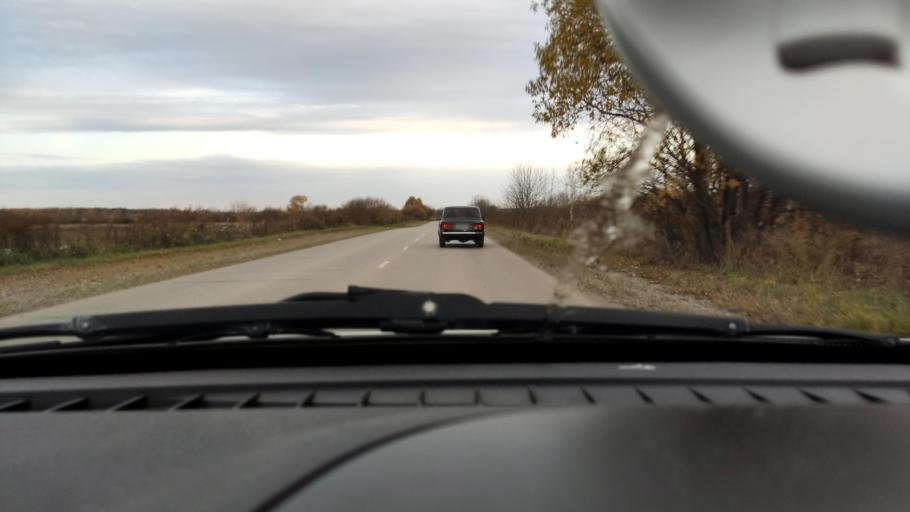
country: RU
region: Perm
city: Kondratovo
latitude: 57.9987
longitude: 56.0773
